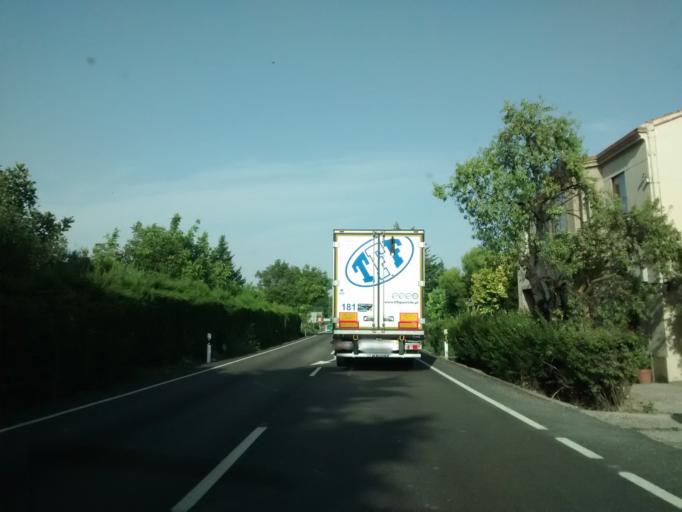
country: ES
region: Aragon
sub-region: Provincia de Zaragoza
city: Malejan
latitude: 41.8292
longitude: -1.5479
